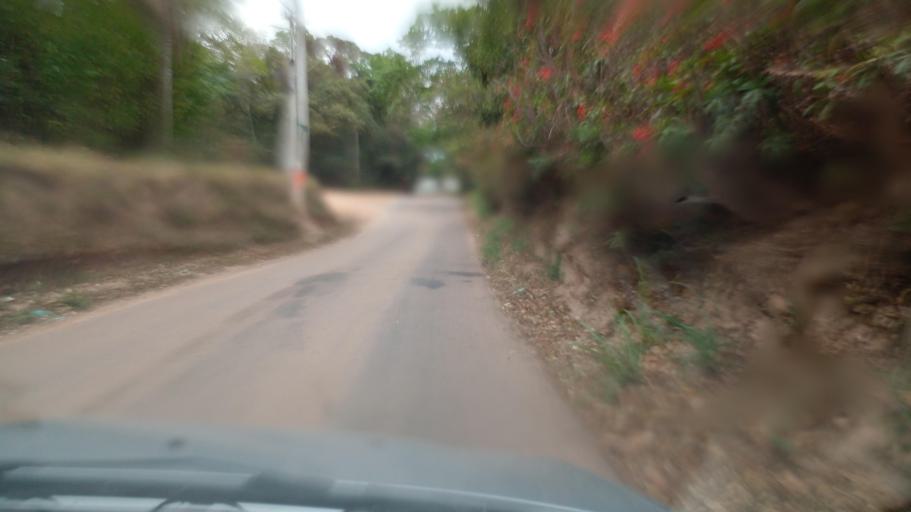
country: BR
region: Sao Paulo
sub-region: Jundiai
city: Jundiai
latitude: -23.1367
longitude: -46.9097
